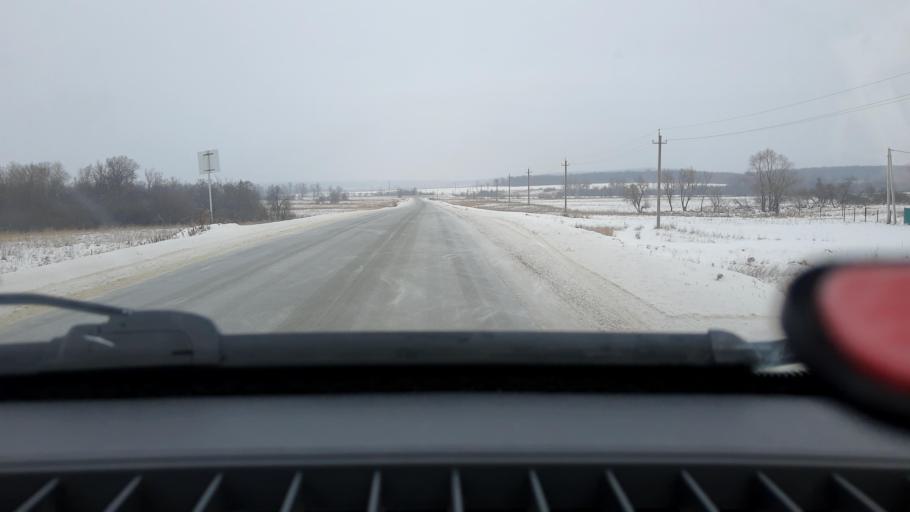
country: RU
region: Bashkortostan
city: Iglino
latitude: 54.7204
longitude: 56.4039
